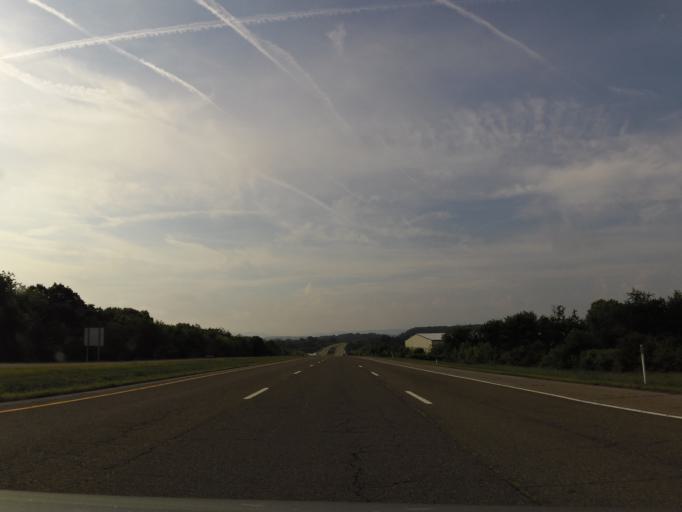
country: US
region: Tennessee
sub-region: Blount County
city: Alcoa
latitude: 35.8326
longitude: -83.9655
